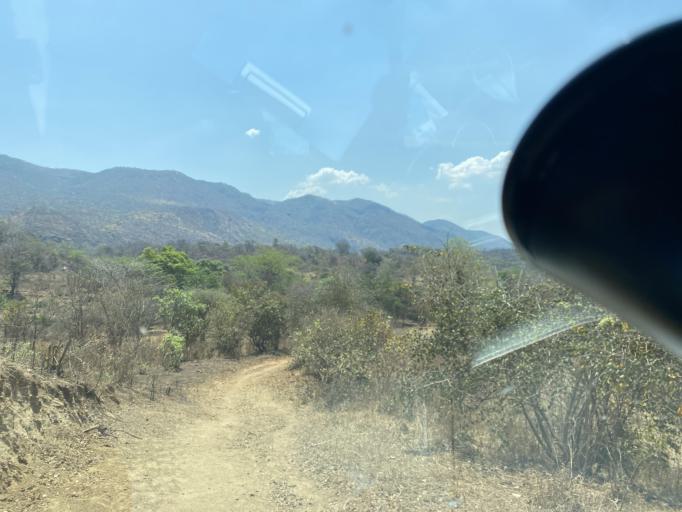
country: ZM
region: Lusaka
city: Kafue
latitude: -15.7768
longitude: 28.4586
